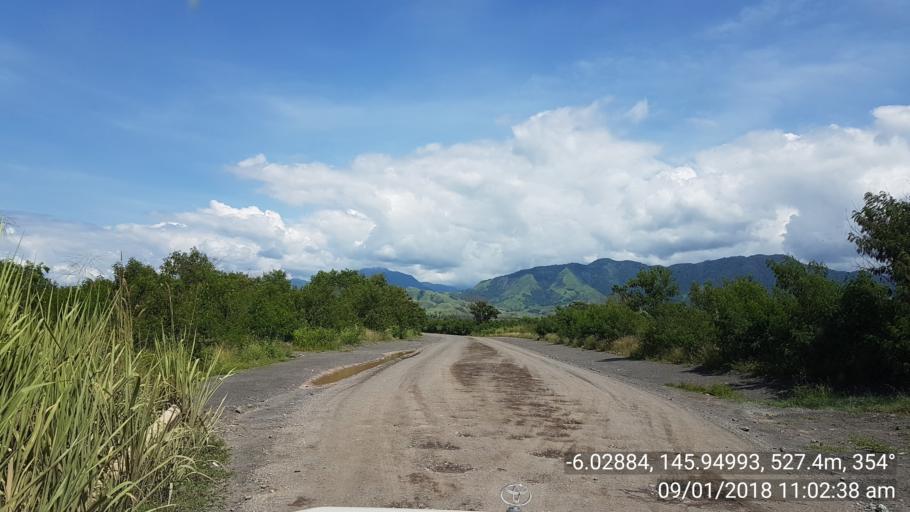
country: PG
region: Eastern Highlands
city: Kainantu
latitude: -6.0290
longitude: 145.9500
